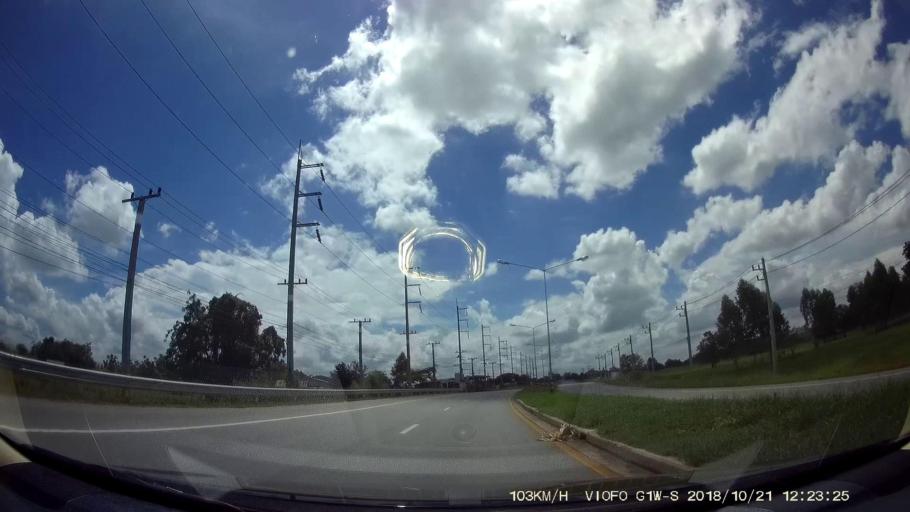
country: TH
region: Nakhon Ratchasima
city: Dan Khun Thot
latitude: 15.2459
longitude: 101.7879
